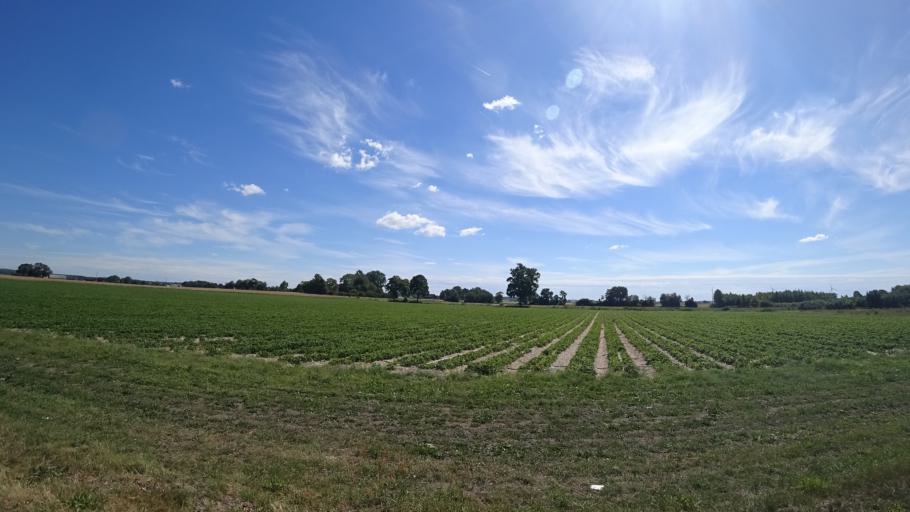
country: SE
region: Skane
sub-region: Kristianstads Kommun
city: Onnestad
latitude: 56.0655
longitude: 14.0272
